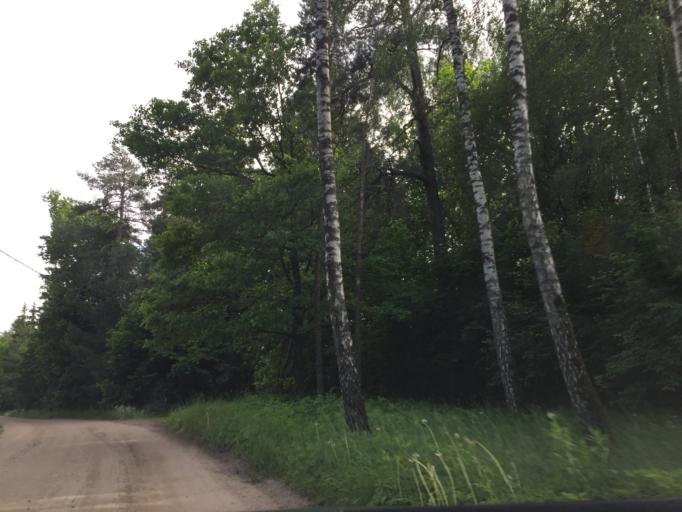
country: LV
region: Stopini
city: Ulbroka
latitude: 56.9292
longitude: 24.2891
